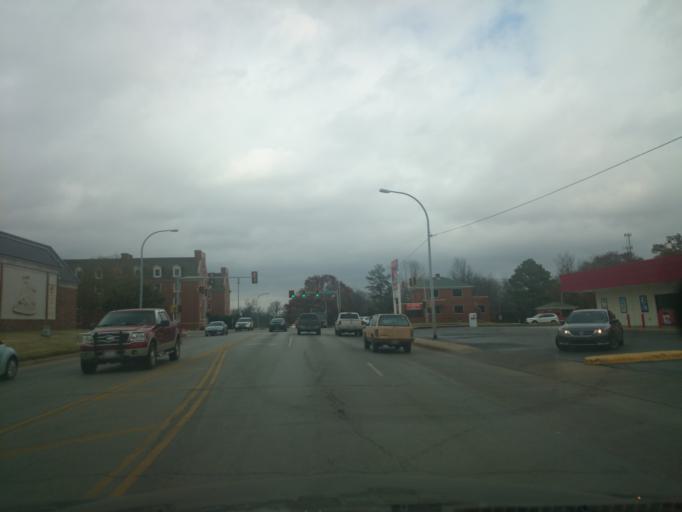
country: US
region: Oklahoma
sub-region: Payne County
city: Stillwater
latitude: 36.1261
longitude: -97.0627
